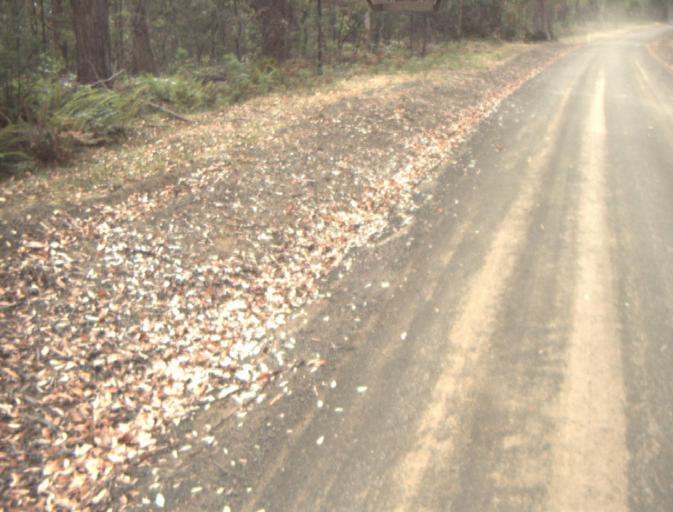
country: AU
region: Tasmania
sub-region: Northern Midlands
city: Evandale
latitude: -41.4944
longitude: 147.5577
